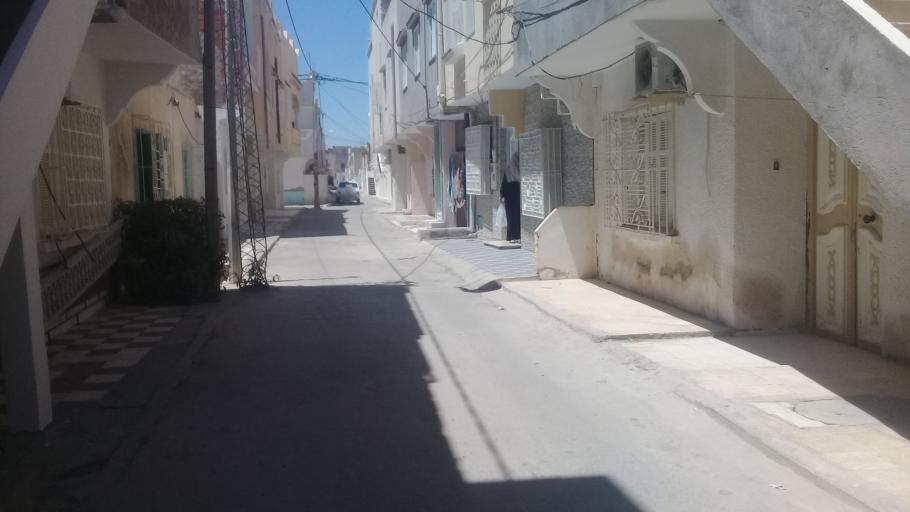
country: TN
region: Al Qayrawan
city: Kairouan
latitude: 35.6693
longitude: 10.0867
